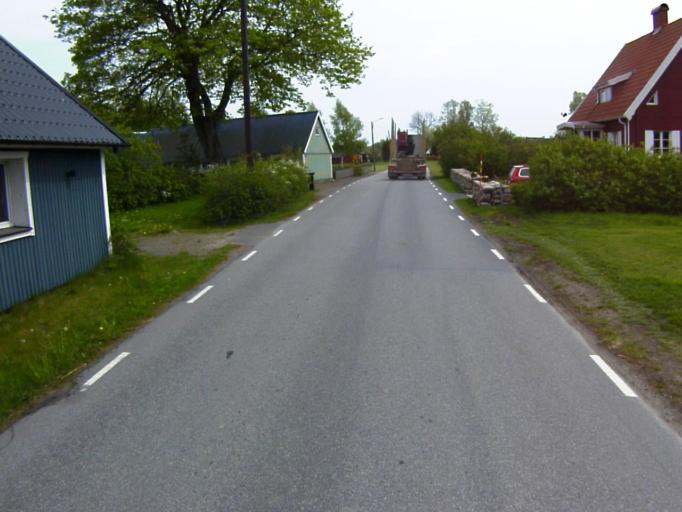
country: SE
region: Skane
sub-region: Kristianstads Kommun
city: Onnestad
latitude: 55.9429
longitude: 13.9505
